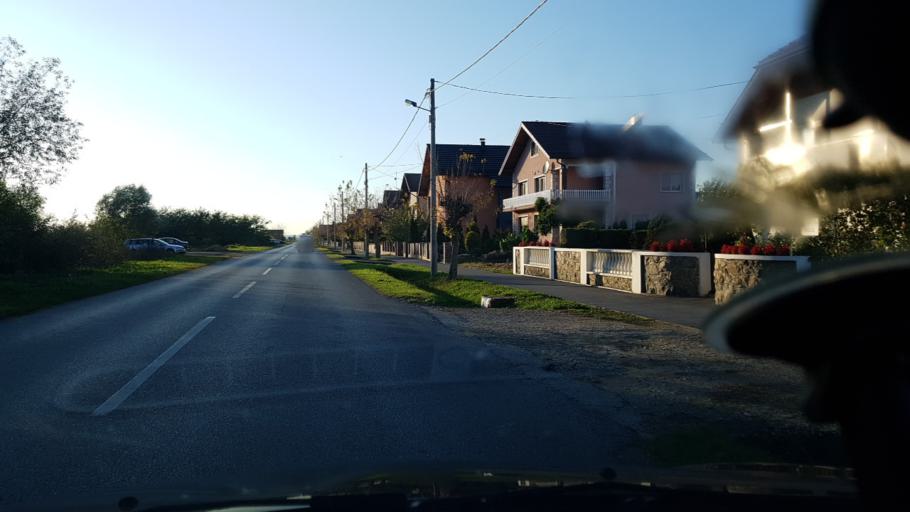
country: HR
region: Koprivnicko-Krizevacka
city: Virje
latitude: 46.0478
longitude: 17.0455
